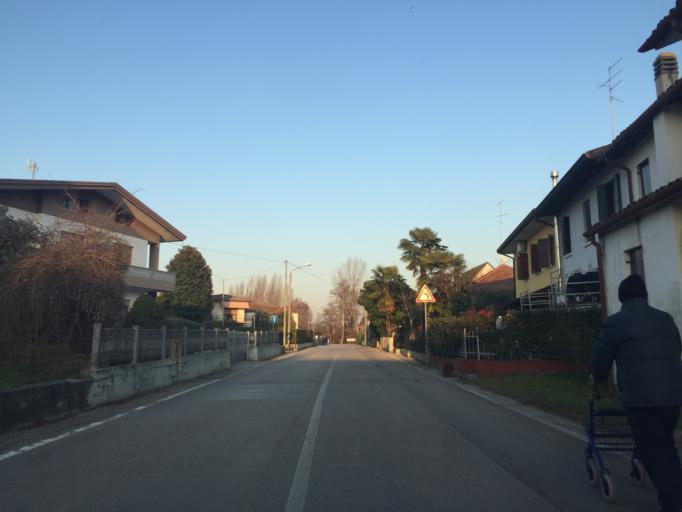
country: IT
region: Friuli Venezia Giulia
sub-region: Provincia di Pordenone
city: Sacile
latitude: 45.9635
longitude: 12.5217
